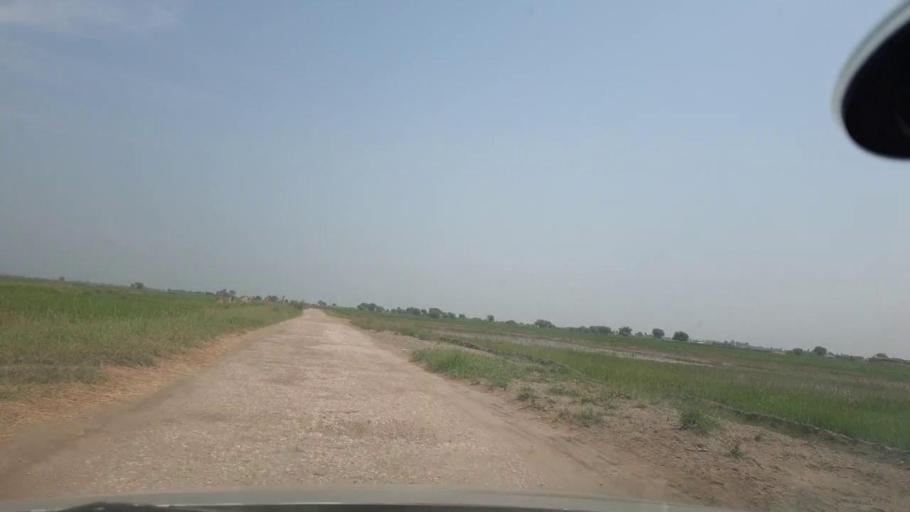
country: PK
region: Sindh
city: Jacobabad
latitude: 28.1400
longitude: 68.3648
